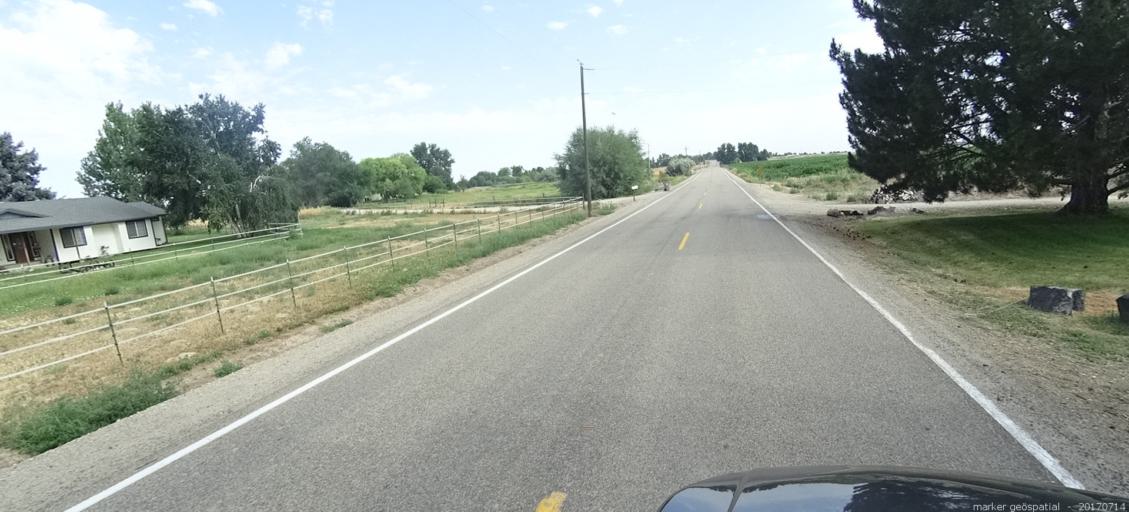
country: US
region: Idaho
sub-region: Ada County
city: Kuna
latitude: 43.4774
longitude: -116.3544
